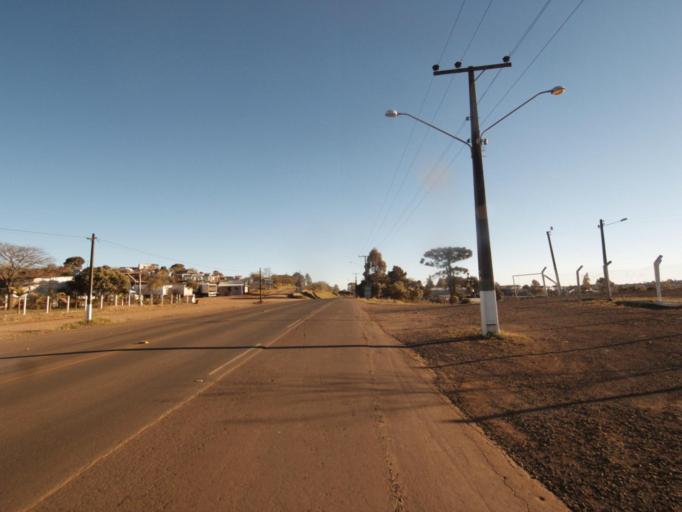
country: AR
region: Misiones
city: Bernardo de Irigoyen
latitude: -26.2667
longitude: -53.6266
